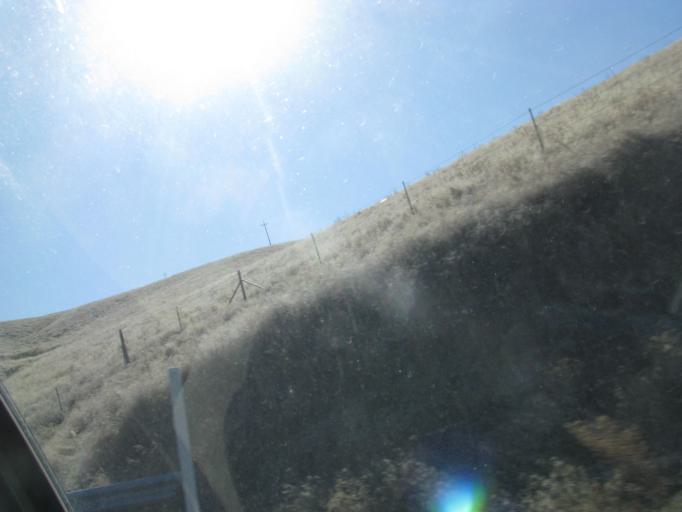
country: US
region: Washington
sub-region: Asotin County
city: Asotin
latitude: 46.3257
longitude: -117.0588
